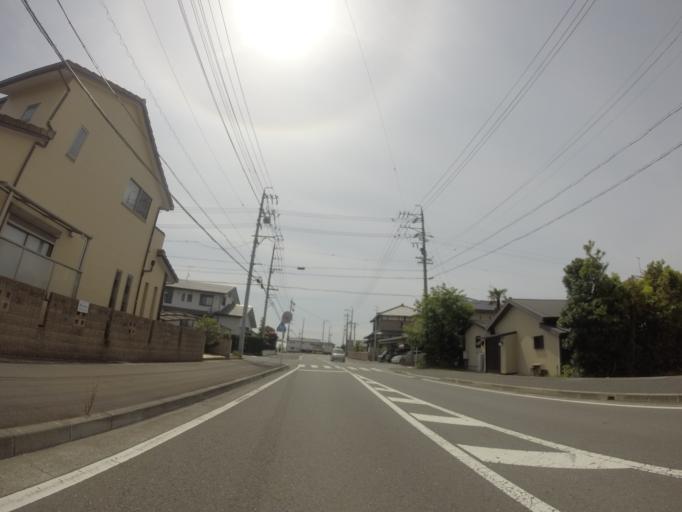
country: JP
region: Shizuoka
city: Fujieda
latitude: 34.8069
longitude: 138.2885
